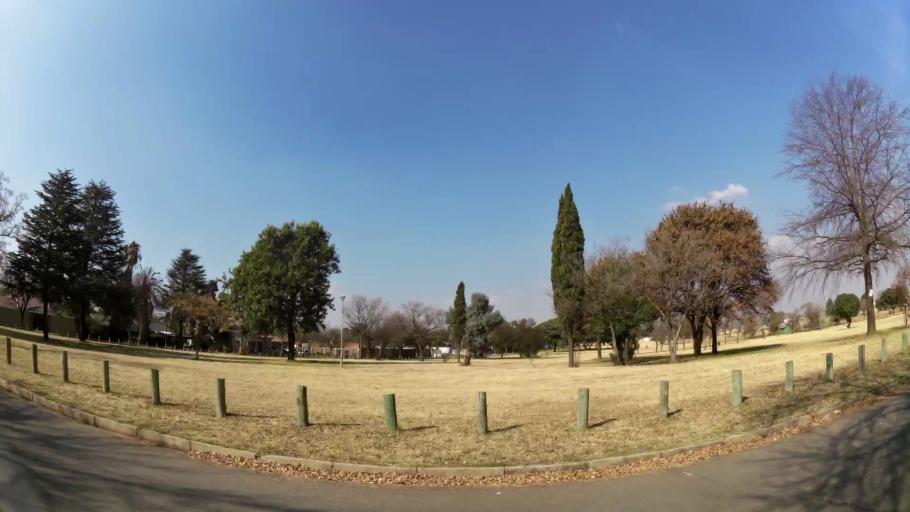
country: ZA
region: Gauteng
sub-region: Ekurhuleni Metropolitan Municipality
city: Boksburg
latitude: -26.1830
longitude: 28.2680
